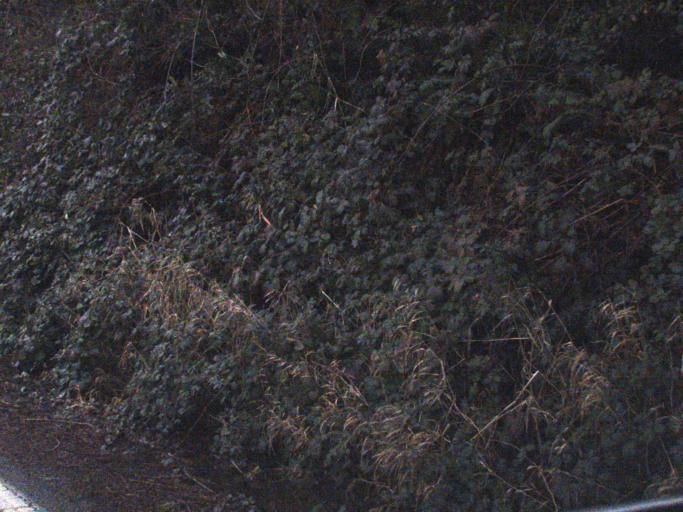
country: US
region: Washington
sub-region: Snohomish County
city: Smokey Point
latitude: 48.1526
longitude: -122.2397
